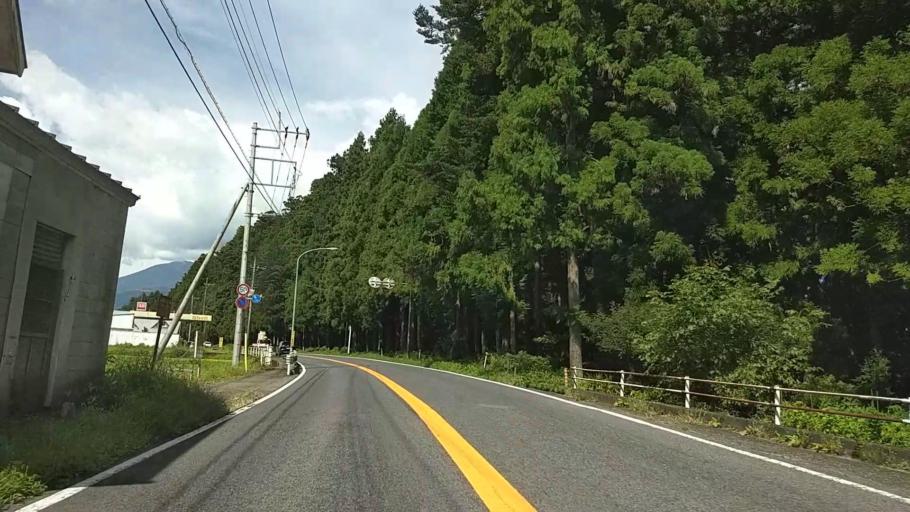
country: JP
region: Tochigi
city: Imaichi
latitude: 36.7301
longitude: 139.6676
